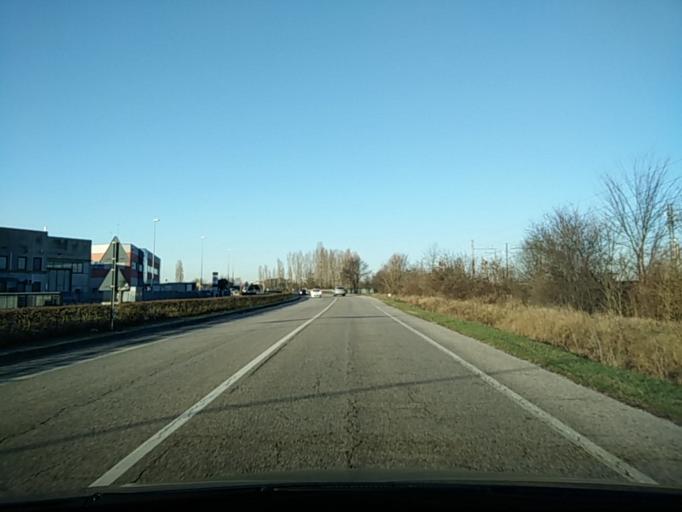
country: IT
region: Veneto
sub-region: Provincia di Venezia
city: Ballo
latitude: 45.4509
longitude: 12.0599
